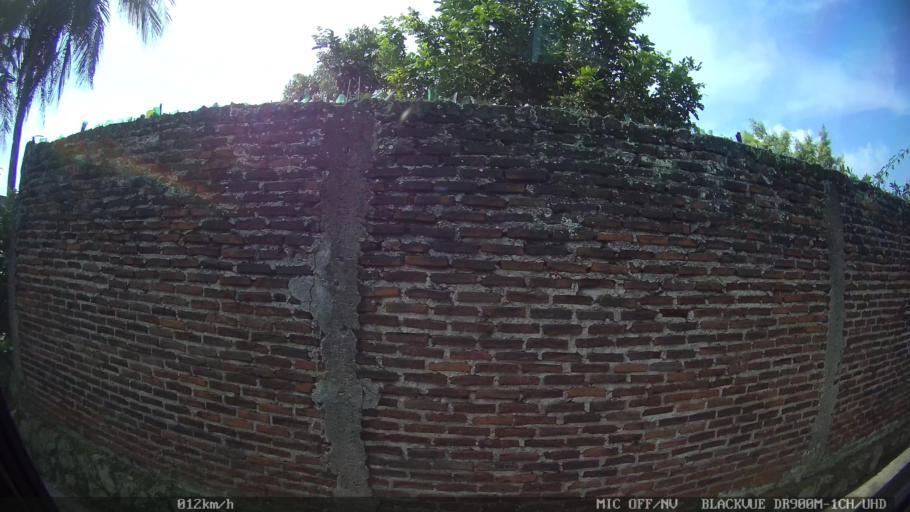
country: ID
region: Lampung
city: Kedaton
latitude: -5.3879
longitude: 105.2325
